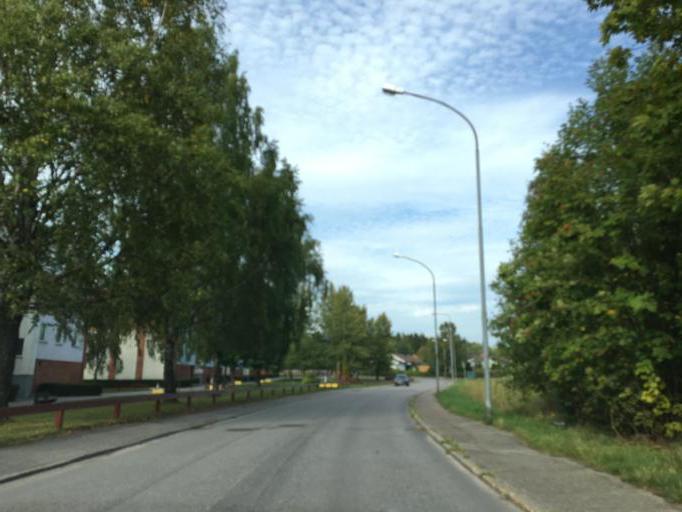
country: SE
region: Soedermanland
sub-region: Eskilstuna Kommun
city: Eskilstuna
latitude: 59.3929
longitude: 16.4982
